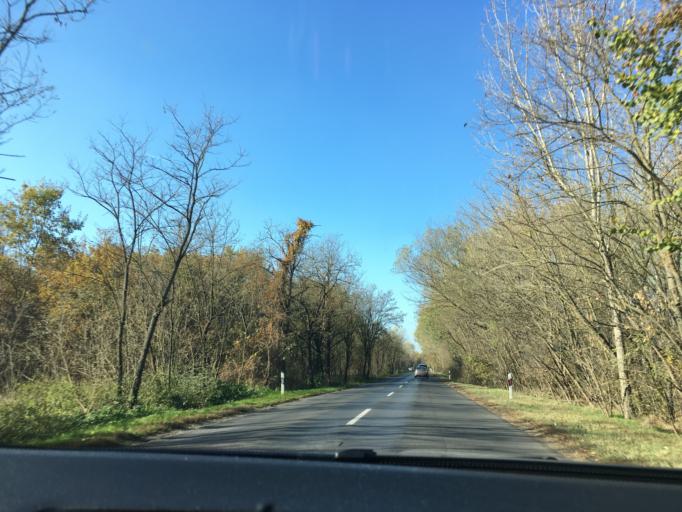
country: HU
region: Hajdu-Bihar
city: Hajdusamson
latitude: 47.5265
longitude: 21.7430
